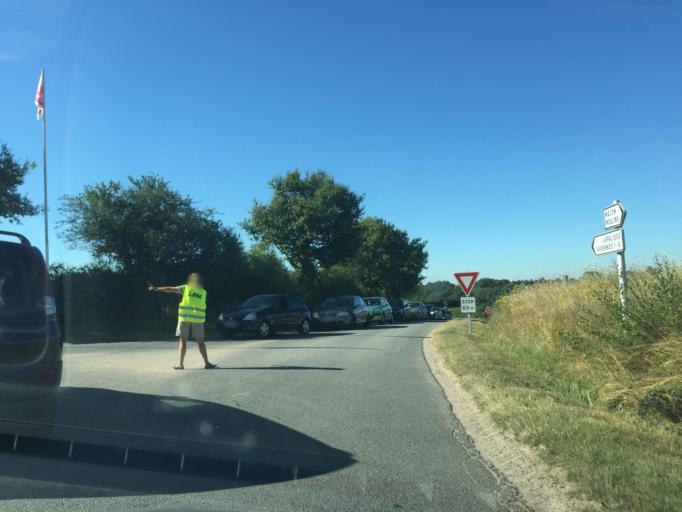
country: FR
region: Auvergne
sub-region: Departement de l'Allier
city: Dompierre-sur-Besbre
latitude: 46.5084
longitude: 3.6225
